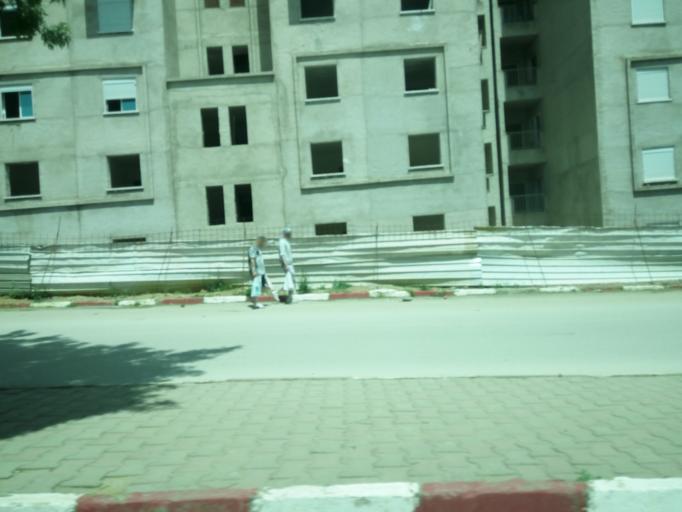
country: DZ
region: Tipaza
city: Saoula
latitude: 36.7320
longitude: 2.9940
